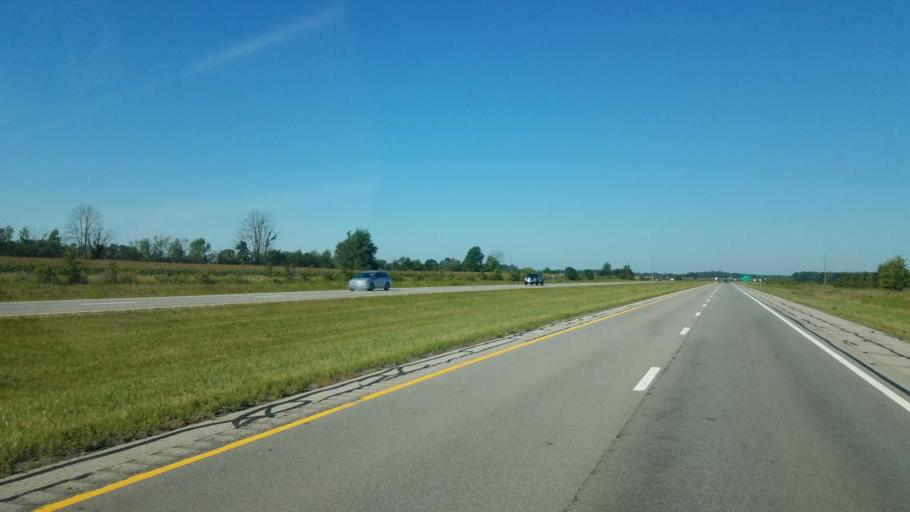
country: US
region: Ohio
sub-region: Crawford County
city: Galion
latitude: 40.7621
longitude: -82.8234
